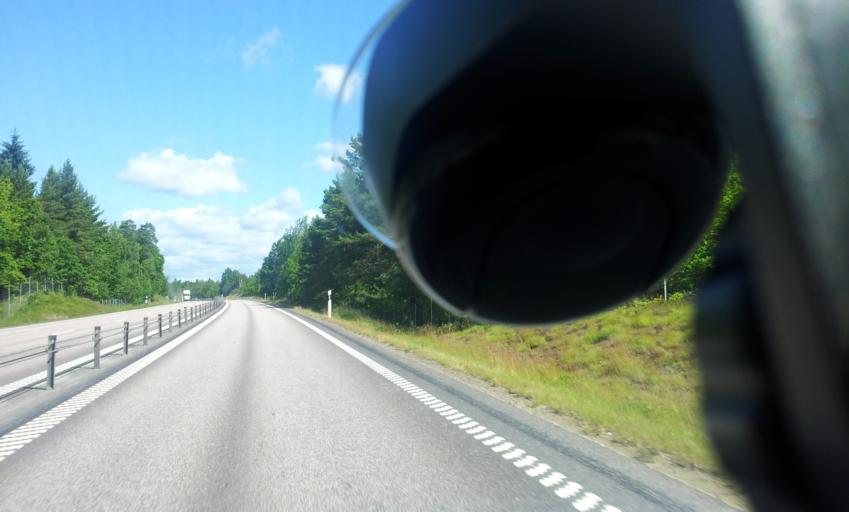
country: SE
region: Kalmar
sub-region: Oskarshamns Kommun
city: Paskallavik
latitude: 57.2028
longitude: 16.4380
